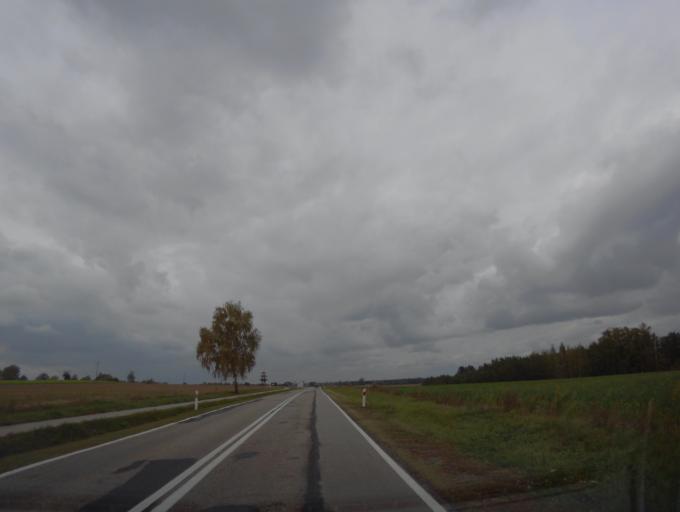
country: PL
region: Lublin Voivodeship
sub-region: Powiat wlodawski
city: Wlodawa
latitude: 51.6543
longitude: 23.5230
